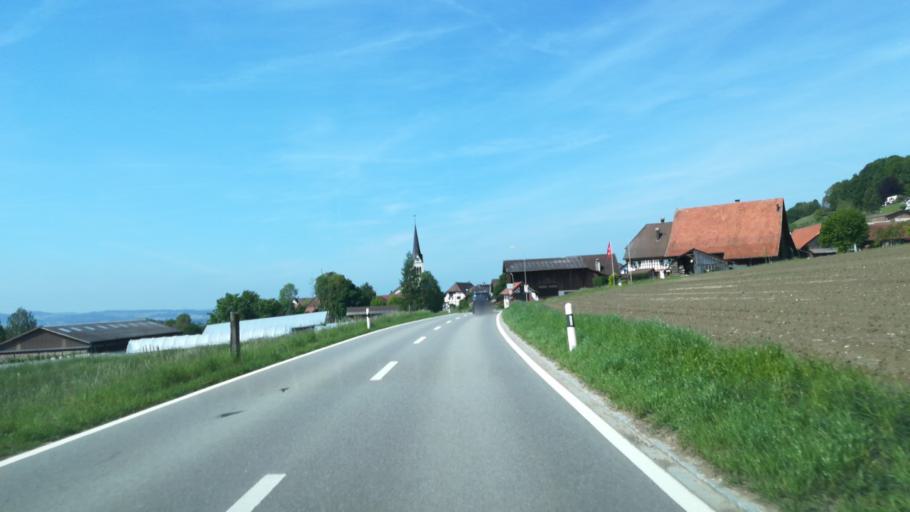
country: CH
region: Thurgau
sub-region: Frauenfeld District
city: Pfyn
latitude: 47.6067
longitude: 8.9143
